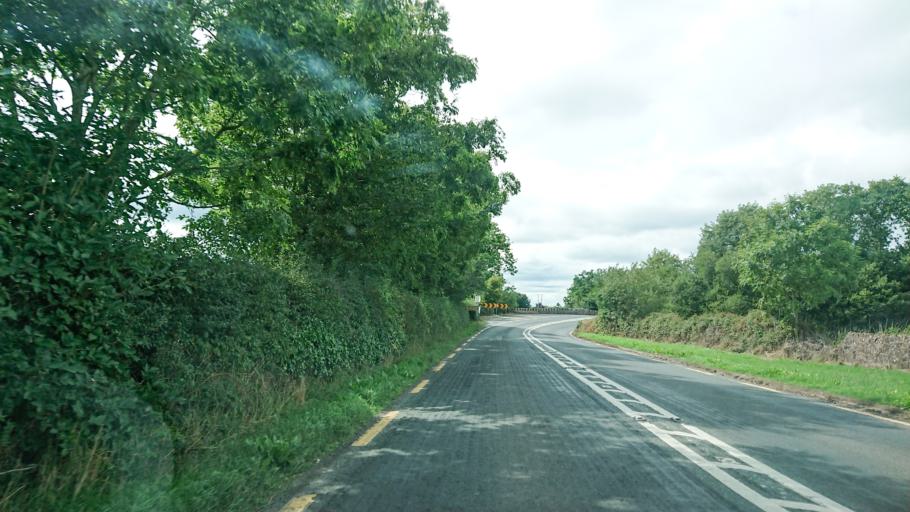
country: IE
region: Munster
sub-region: Waterford
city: Dungarvan
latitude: 52.1215
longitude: -7.7624
